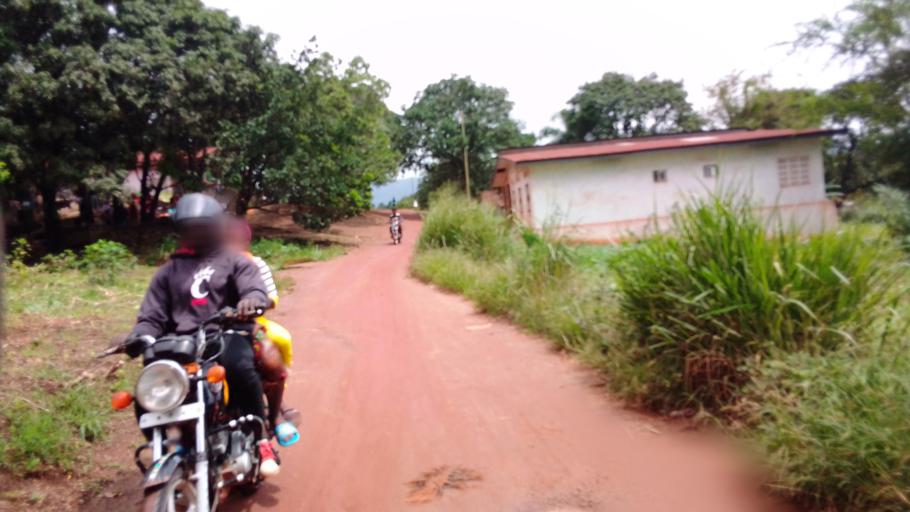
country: SL
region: Eastern Province
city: Kenema
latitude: 7.8661
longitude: -11.1789
